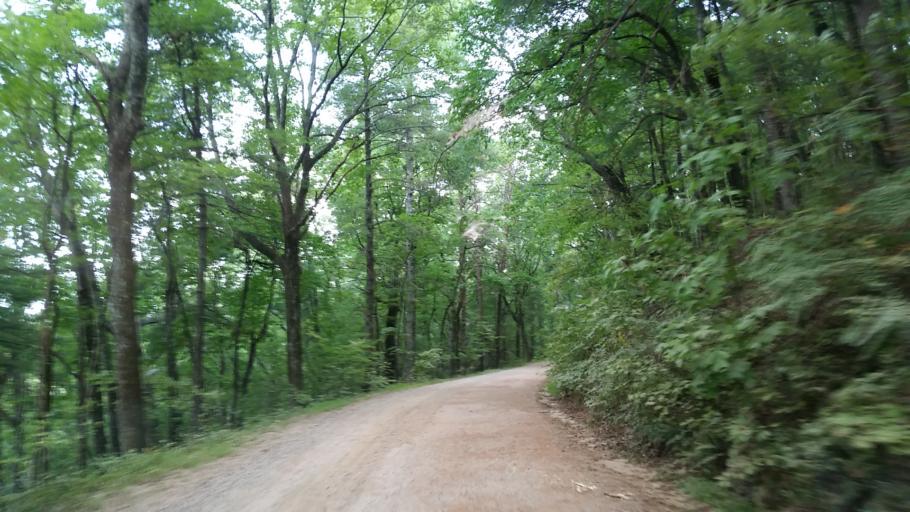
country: US
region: Georgia
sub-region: Lumpkin County
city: Dahlonega
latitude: 34.6337
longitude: -84.1002
